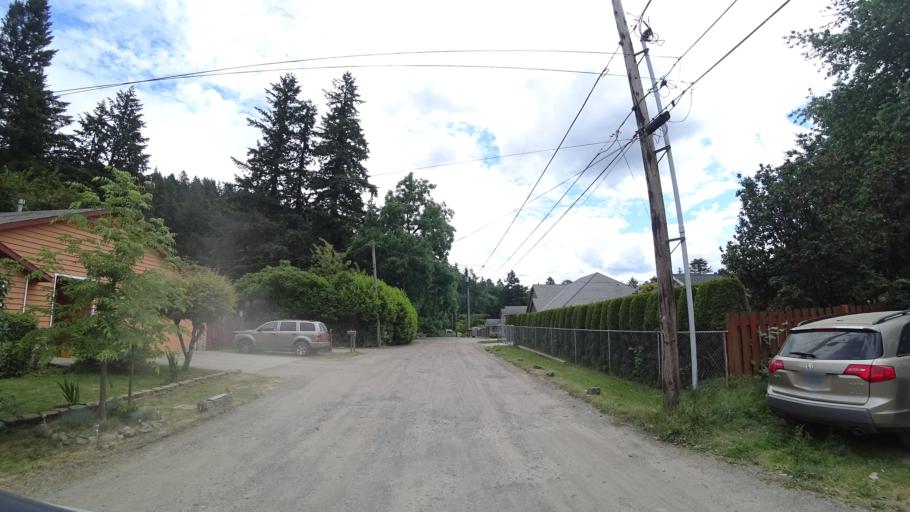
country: US
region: Oregon
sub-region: Clackamas County
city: Happy Valley
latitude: 45.4918
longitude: -122.5182
